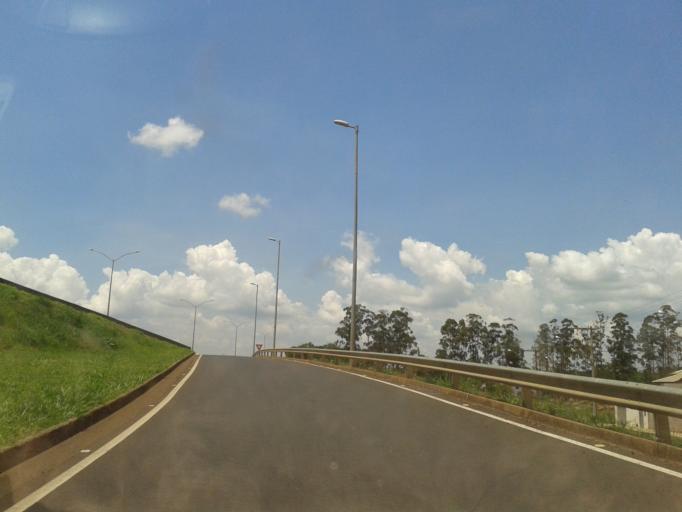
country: BR
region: Minas Gerais
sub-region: Araguari
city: Araguari
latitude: -18.6745
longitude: -48.1785
